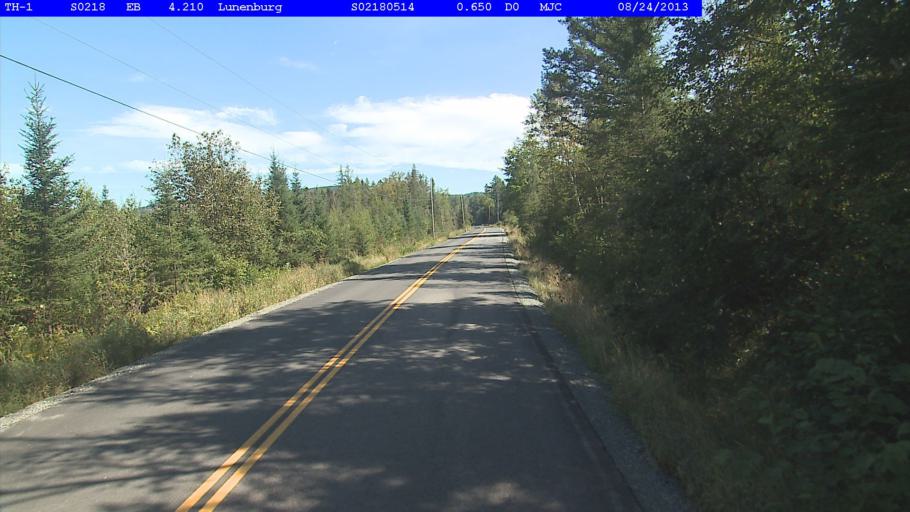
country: US
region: New Hampshire
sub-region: Grafton County
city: Littleton
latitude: 44.4150
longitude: -71.7378
